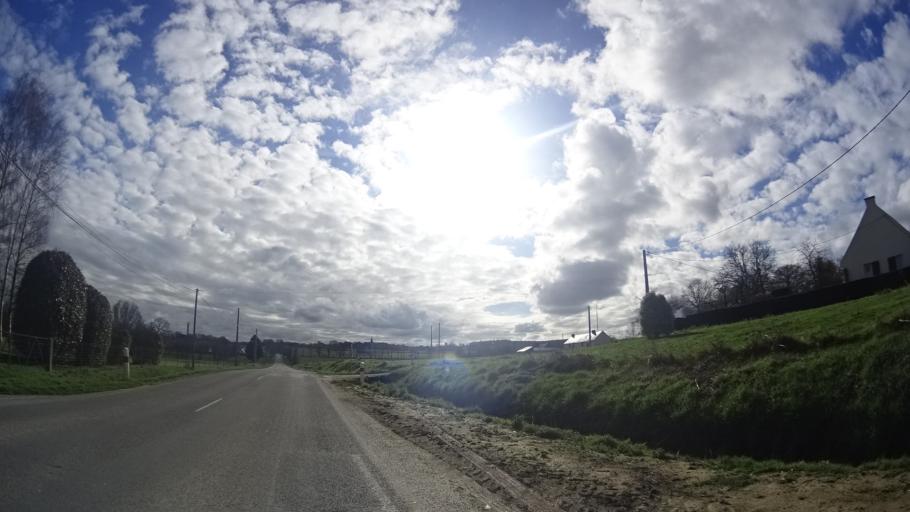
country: FR
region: Brittany
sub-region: Departement des Cotes-d'Armor
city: Plouasne
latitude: 48.3119
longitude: -1.9512
